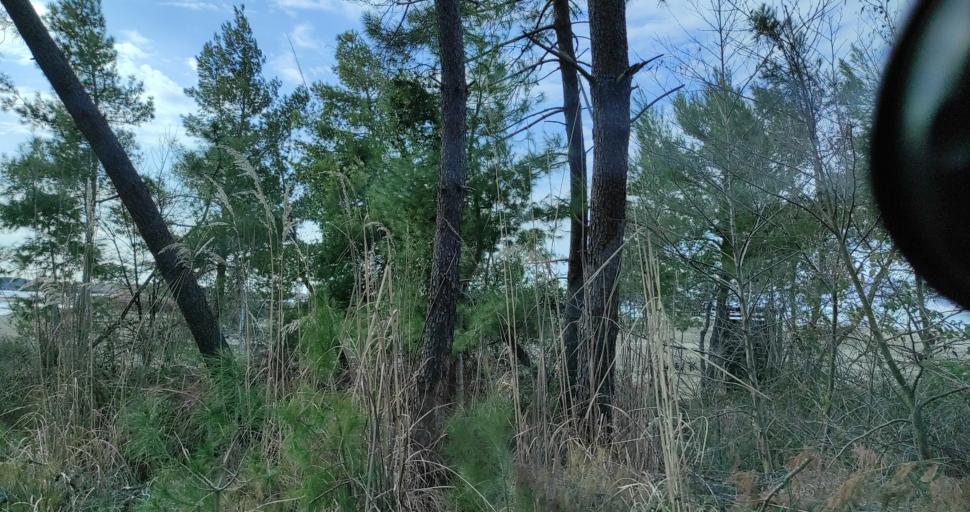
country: AL
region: Lezhe
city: Shengjin
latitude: 41.7666
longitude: 19.5978
